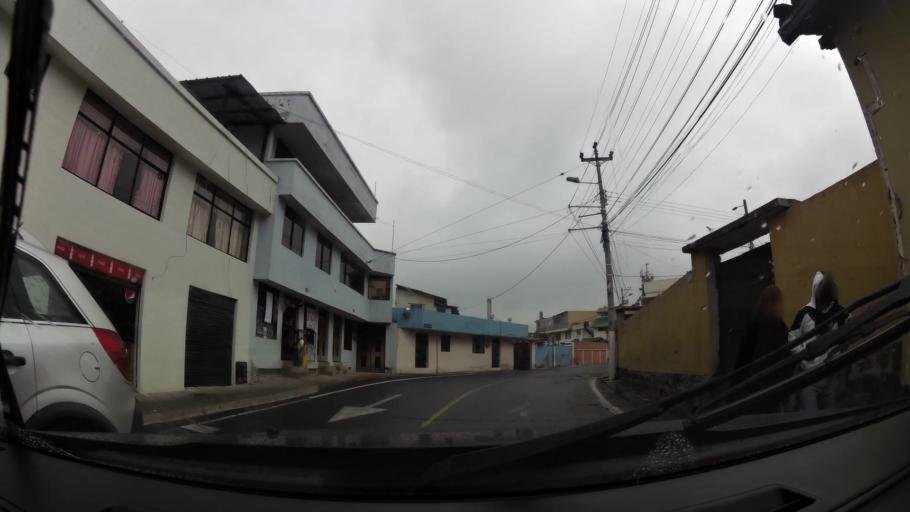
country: EC
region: Pichincha
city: Sangolqui
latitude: -0.2853
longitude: -78.4418
